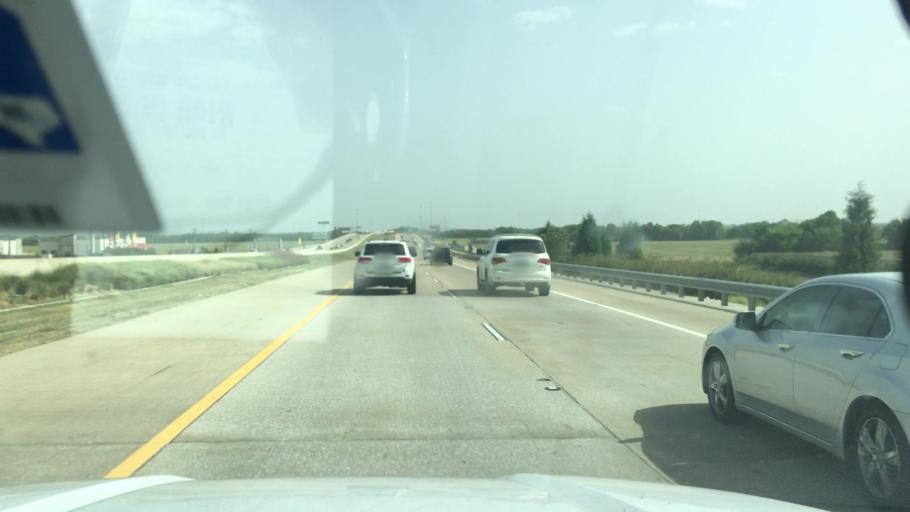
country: US
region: Texas
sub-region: Dallas County
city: Grand Prairie
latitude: 32.6909
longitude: -97.0245
